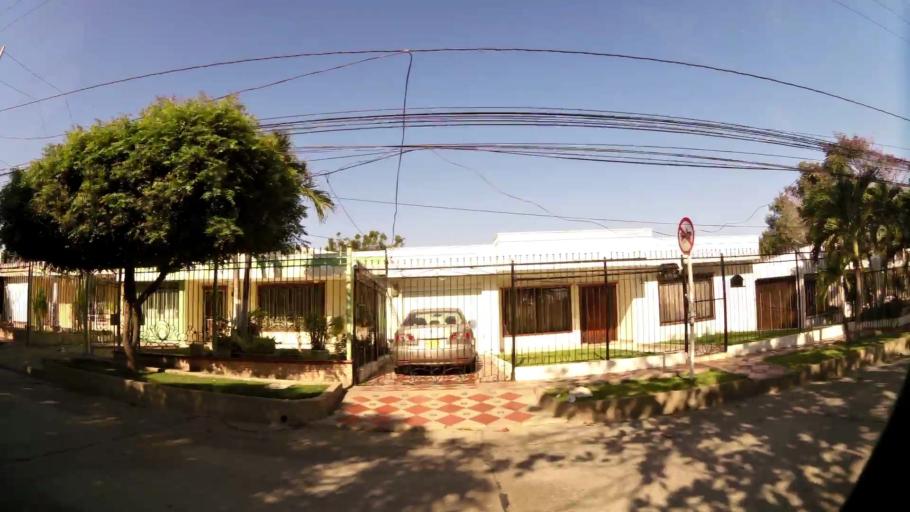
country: CO
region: Atlantico
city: Barranquilla
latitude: 11.0157
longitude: -74.8038
